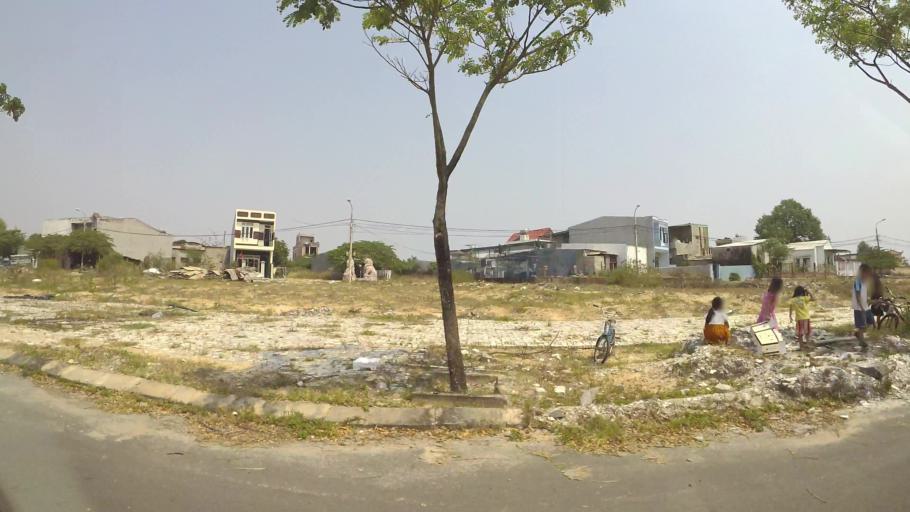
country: VN
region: Da Nang
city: Ngu Hanh Son
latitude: 16.0060
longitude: 108.2557
